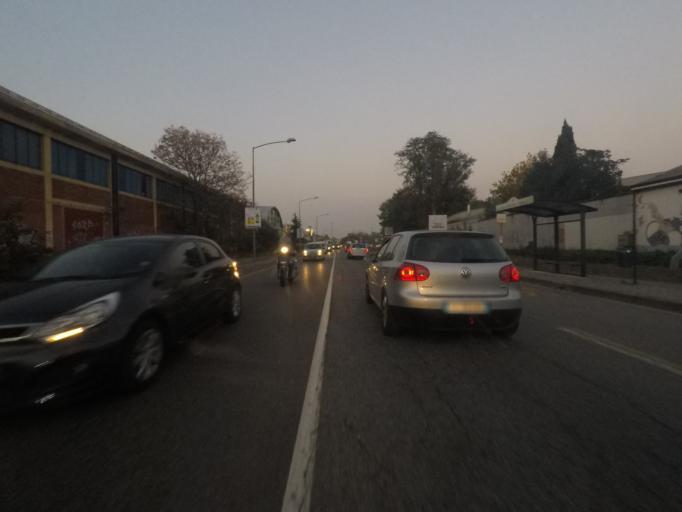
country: IT
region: Lombardy
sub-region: Provincia di Monza e Brianza
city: Brugherio
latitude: 45.5624
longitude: 9.3043
